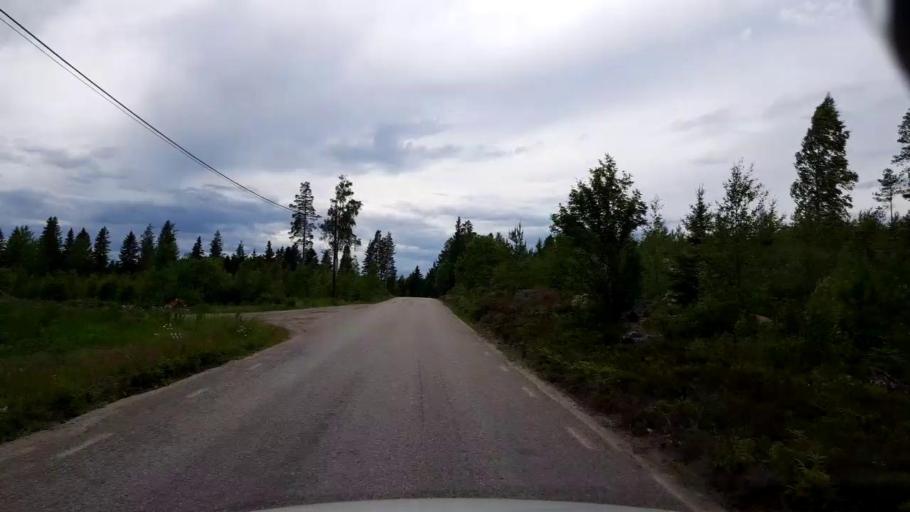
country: SE
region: Gaevleborg
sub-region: Hudiksvalls Kommun
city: Delsbo
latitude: 61.8069
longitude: 16.4701
